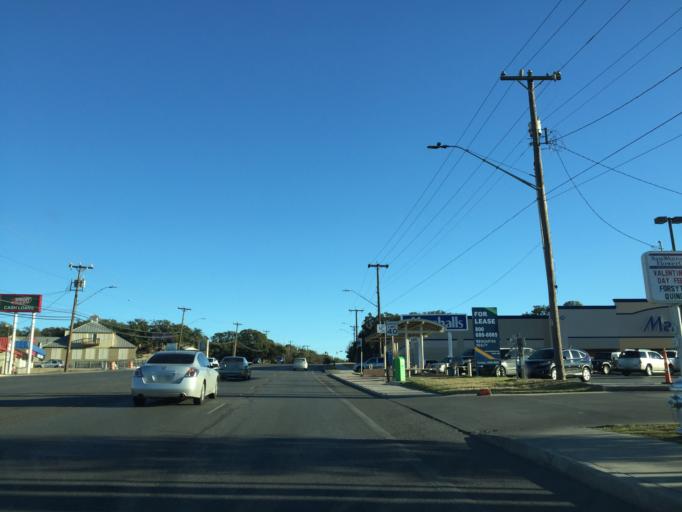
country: US
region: Texas
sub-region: Bexar County
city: Castle Hills
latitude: 29.5458
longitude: -98.5085
